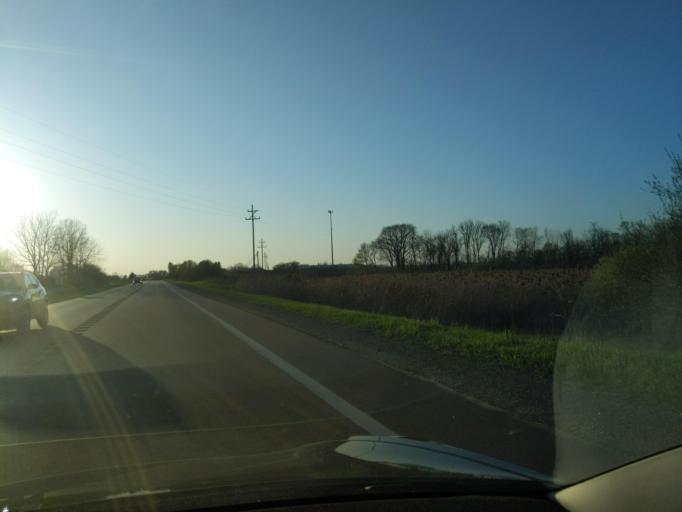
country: US
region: Michigan
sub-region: Ingham County
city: Stockbridge
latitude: 42.4094
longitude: -84.1278
